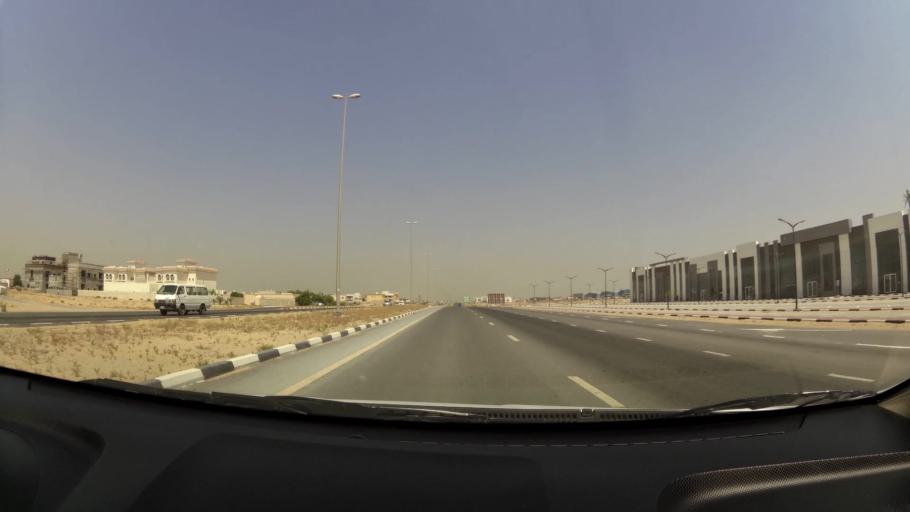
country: AE
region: Ajman
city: Ajman
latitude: 25.4242
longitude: 55.5277
